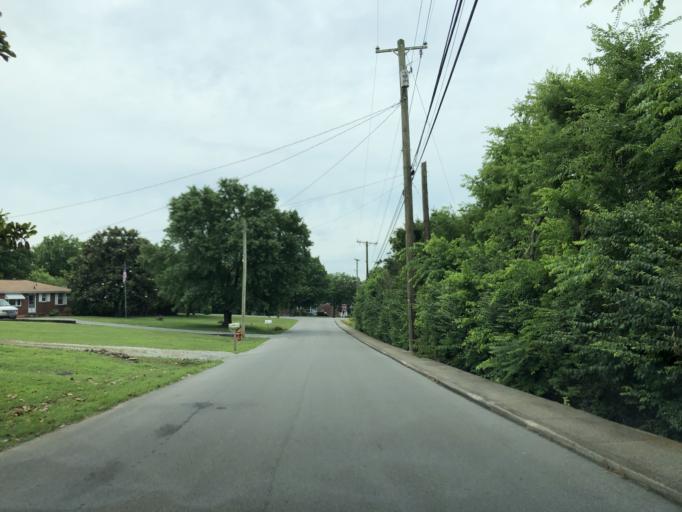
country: US
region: Tennessee
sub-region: Davidson County
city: Goodlettsville
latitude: 36.2894
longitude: -86.7106
